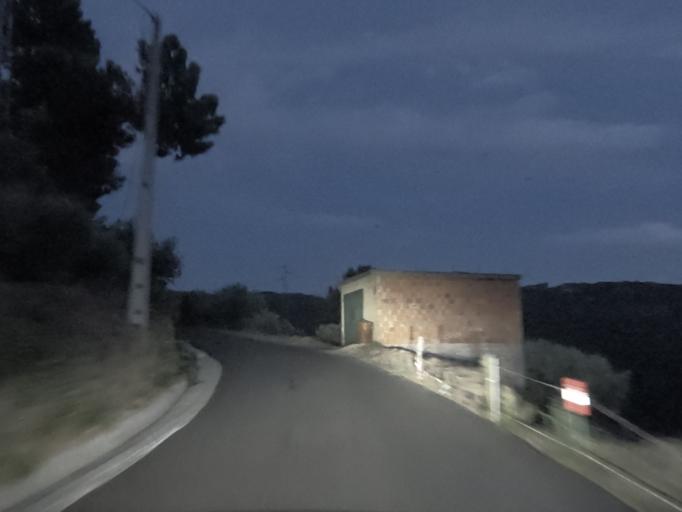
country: PT
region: Vila Real
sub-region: Vila Real
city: Vila Real
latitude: 41.2757
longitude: -7.7590
